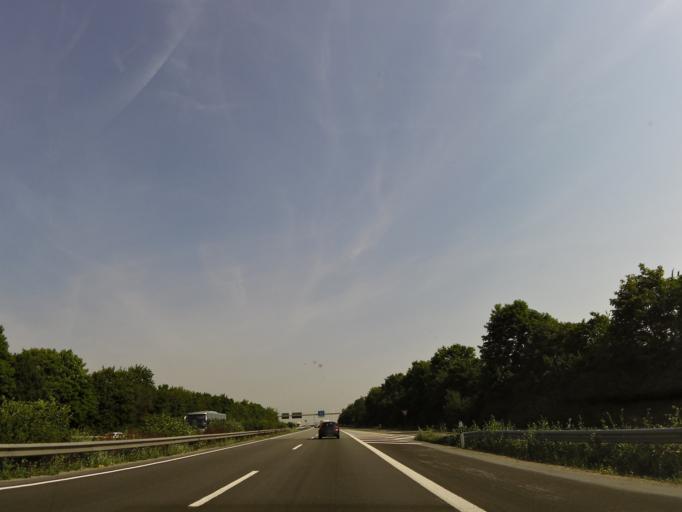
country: DE
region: Rheinland-Pfalz
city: Kleinniedesheim
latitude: 49.6270
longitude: 8.2948
